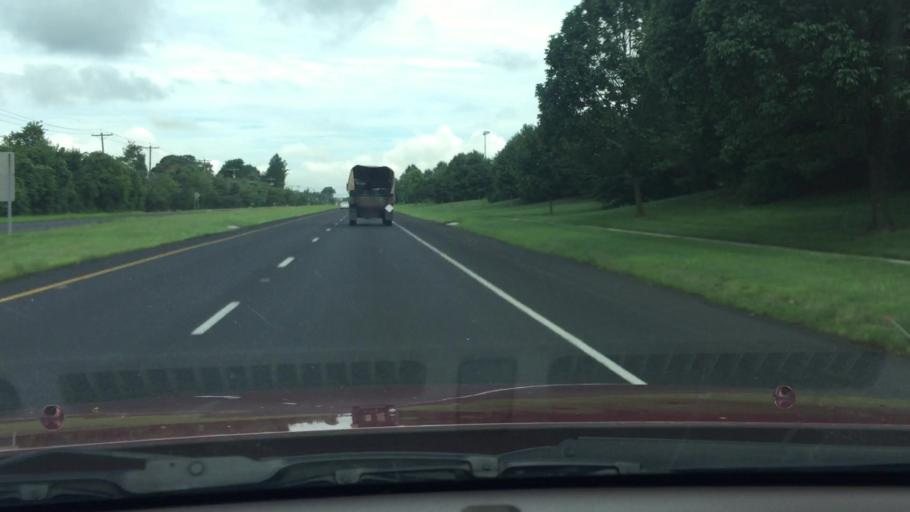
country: US
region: New Jersey
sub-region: Burlington County
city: Bordentown
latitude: 40.0851
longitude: -74.6717
